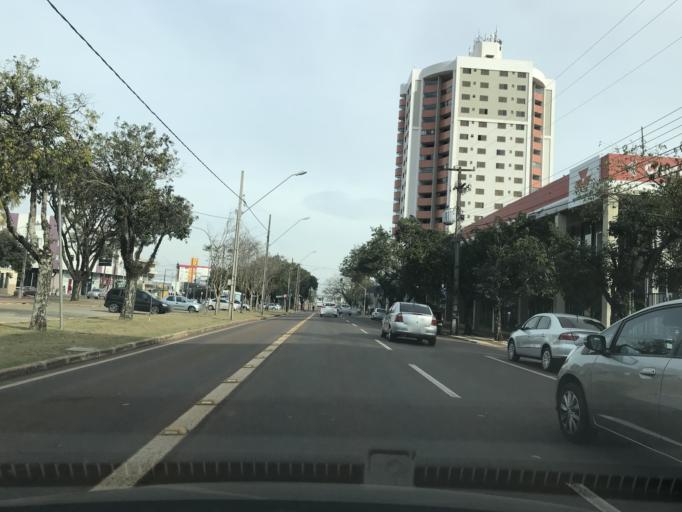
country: BR
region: Parana
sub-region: Cascavel
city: Cascavel
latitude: -24.9545
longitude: -53.4729
